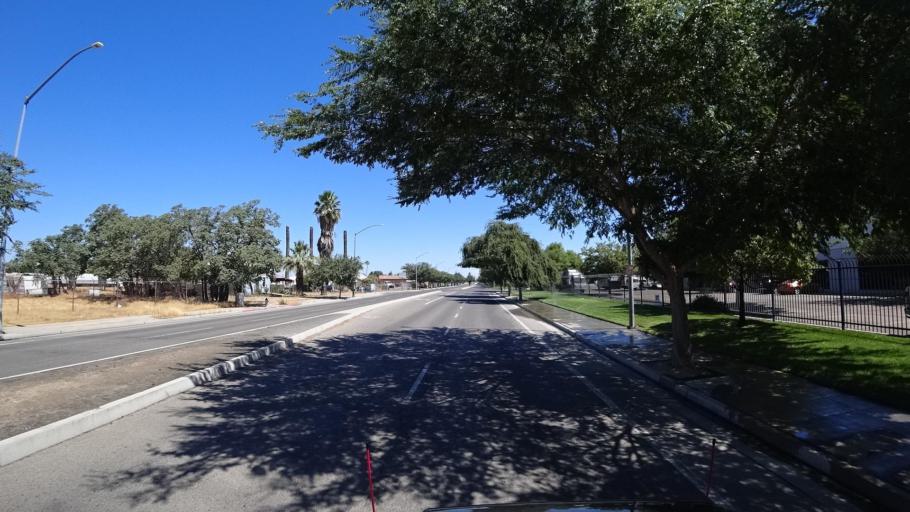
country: US
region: California
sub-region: Fresno County
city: Easton
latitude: 36.6952
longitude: -119.7907
